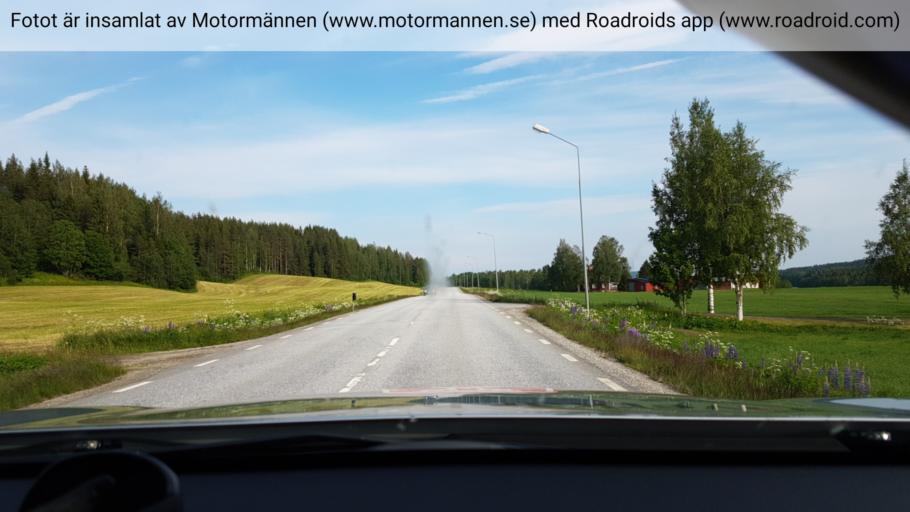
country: SE
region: Vaesterbotten
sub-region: Vindelns Kommun
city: Vindeln
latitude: 64.1370
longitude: 19.5267
